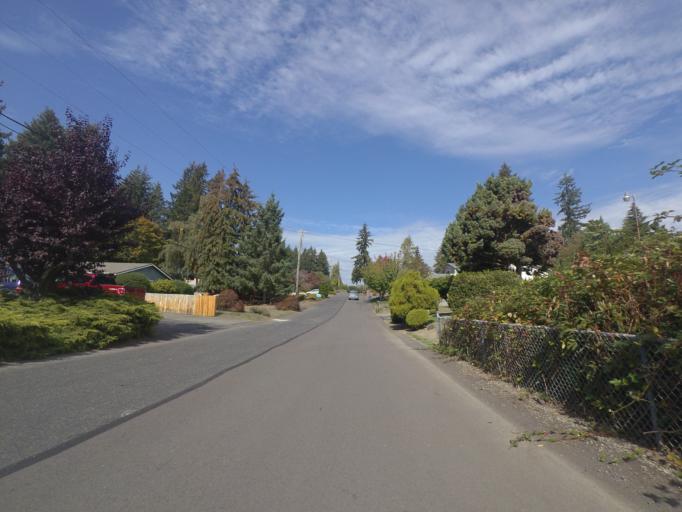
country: US
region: Washington
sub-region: Pierce County
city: Fircrest
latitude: 47.2153
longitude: -122.5289
